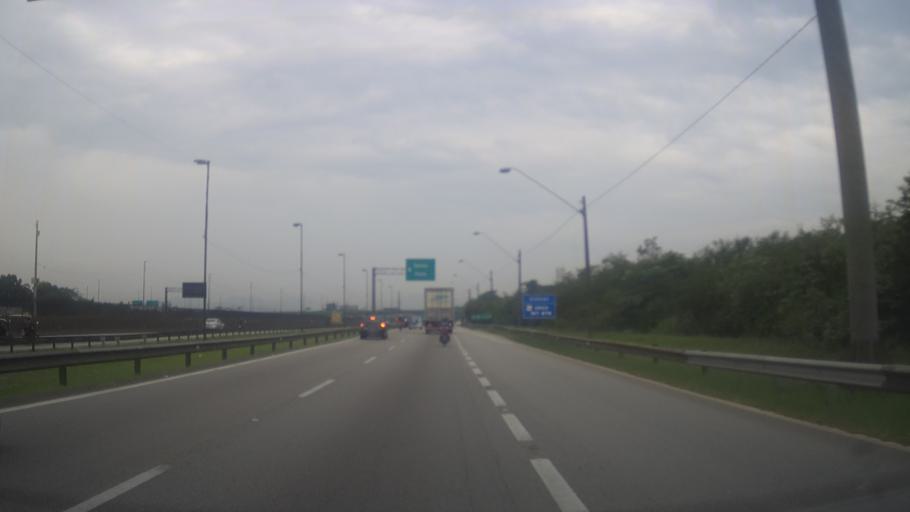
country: BR
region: Sao Paulo
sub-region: Cubatao
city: Cubatao
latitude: -23.9206
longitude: -46.4134
